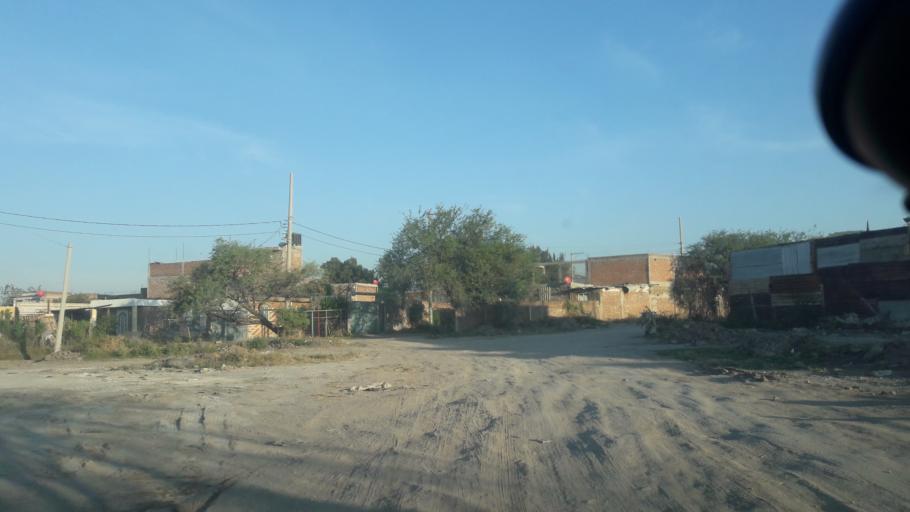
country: MX
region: Guanajuato
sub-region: Leon
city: Medina
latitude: 21.1659
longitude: -101.6354
